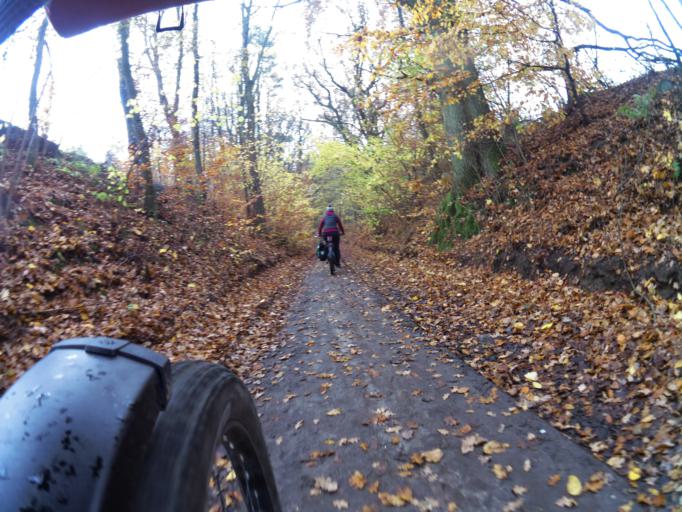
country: PL
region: Pomeranian Voivodeship
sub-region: Powiat pucki
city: Krokowa
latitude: 54.7827
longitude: 18.0882
